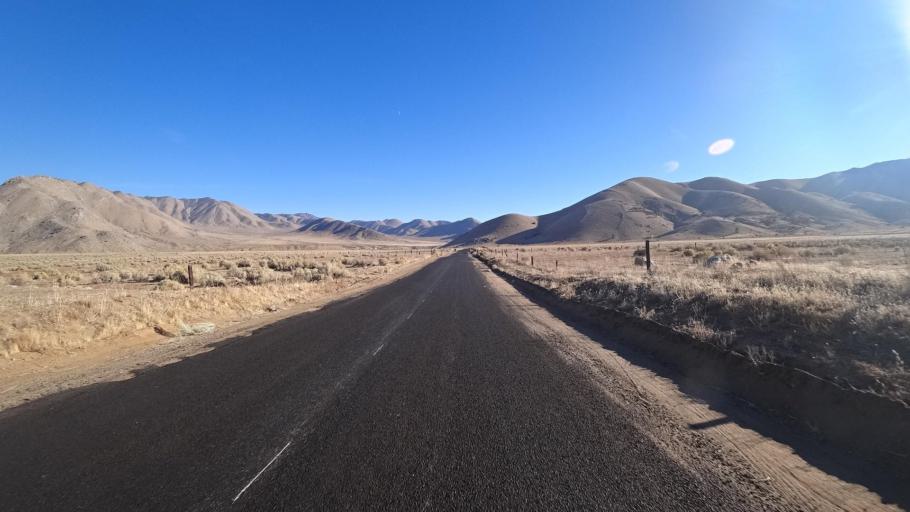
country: US
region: California
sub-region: Kern County
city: Weldon
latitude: 35.6251
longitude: -118.2609
